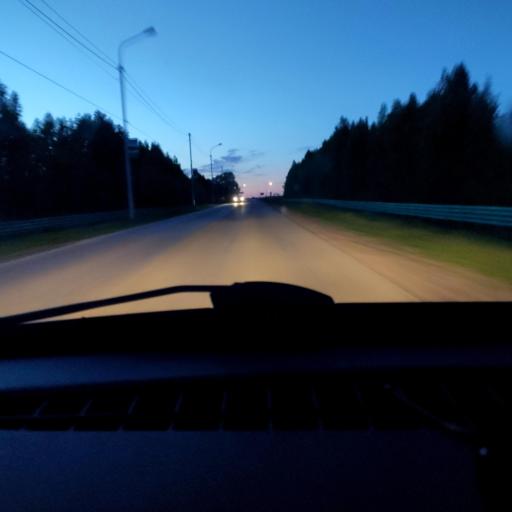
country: RU
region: Bashkortostan
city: Karmaskaly
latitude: 54.3809
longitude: 56.1778
